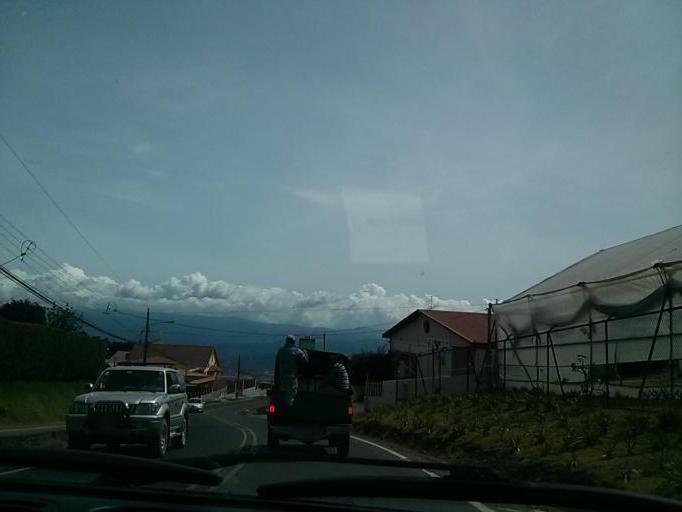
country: CR
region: Cartago
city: Cot
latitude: 9.9192
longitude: -83.8796
